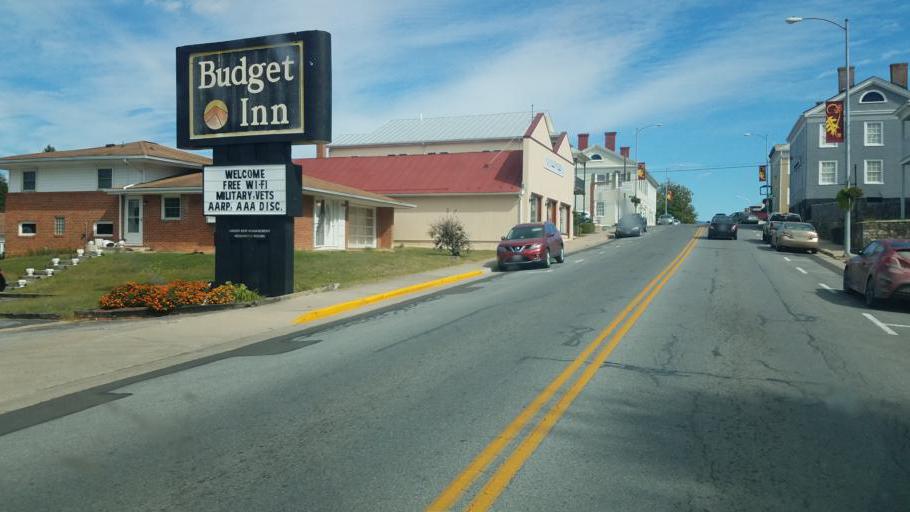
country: US
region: Virginia
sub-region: Page County
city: Luray
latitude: 38.6656
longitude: -78.4656
